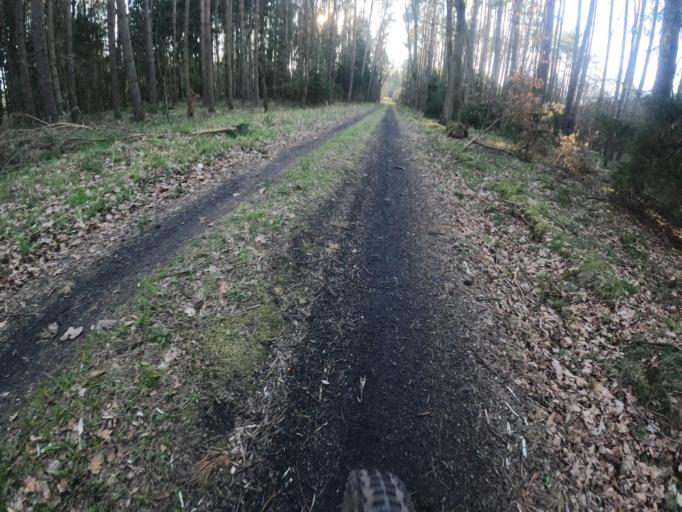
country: PL
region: West Pomeranian Voivodeship
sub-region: Powiat gryficki
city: Brojce
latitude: 53.9567
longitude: 15.4078
